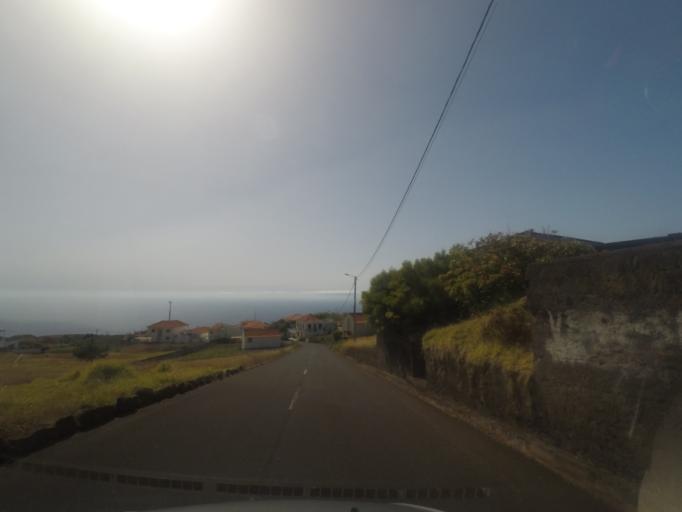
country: PT
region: Madeira
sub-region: Calheta
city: Faja da Ovelha
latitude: 32.8140
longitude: -17.2466
